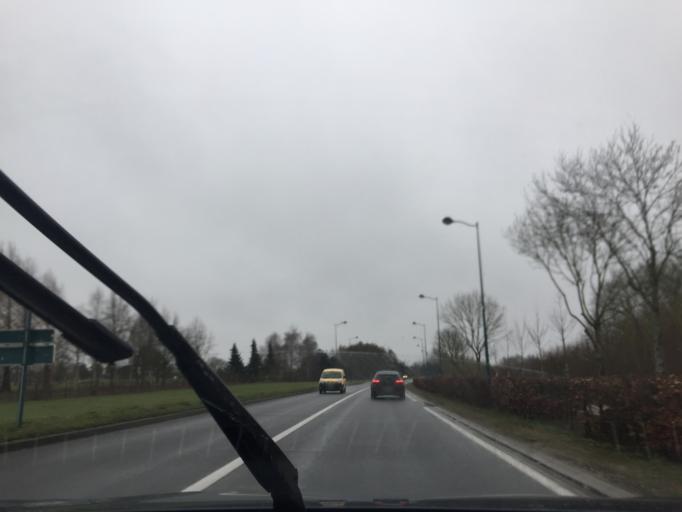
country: FR
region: Ile-de-France
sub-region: Departement de Seine-et-Marne
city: Magny-le-Hongre
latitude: 48.8602
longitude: 2.8062
